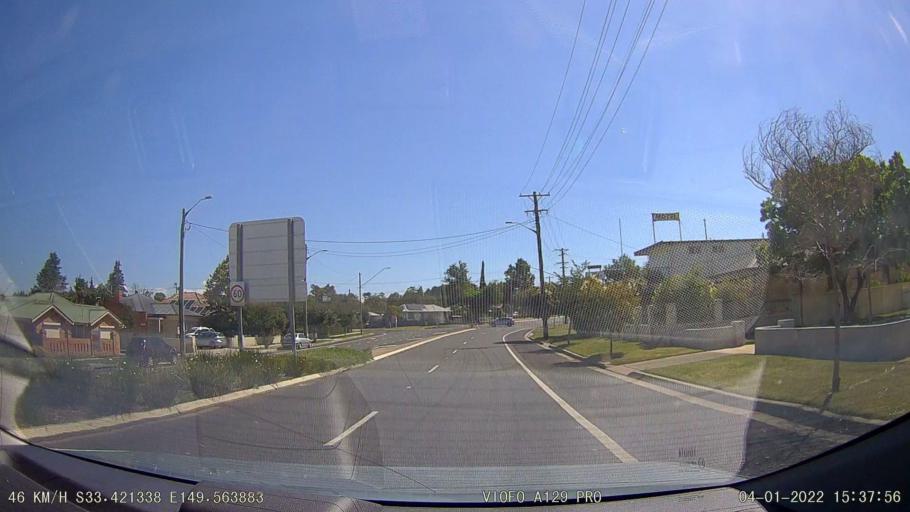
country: AU
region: New South Wales
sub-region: Bathurst Regional
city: Bathurst
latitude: -33.4212
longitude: 149.5641
